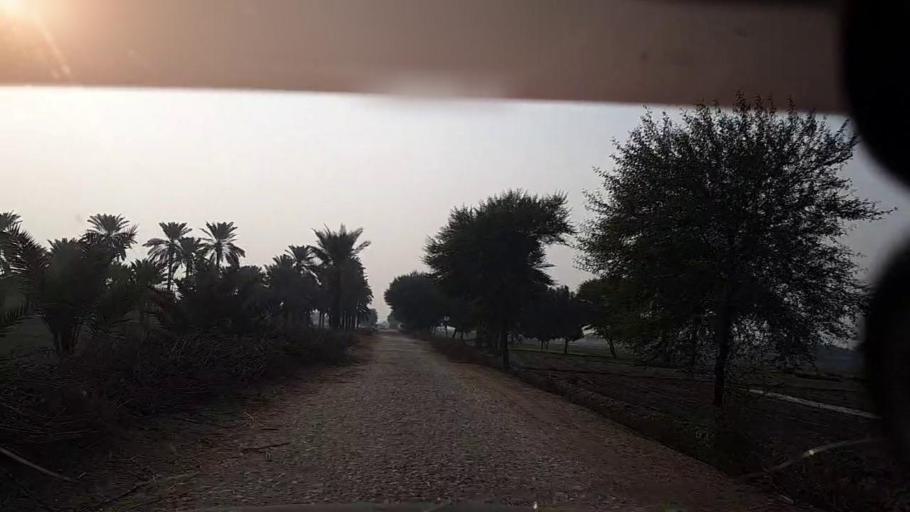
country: PK
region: Sindh
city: Kot Diji
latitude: 27.4374
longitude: 68.6270
